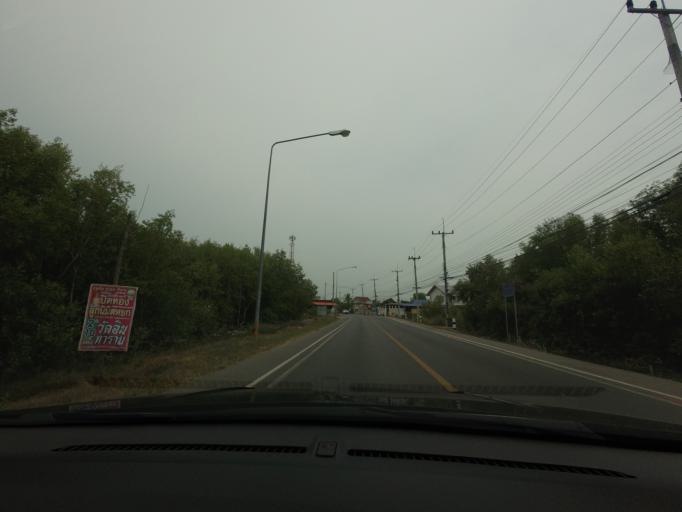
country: TH
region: Phetchaburi
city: Ban Laem
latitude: 13.2667
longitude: 99.9369
